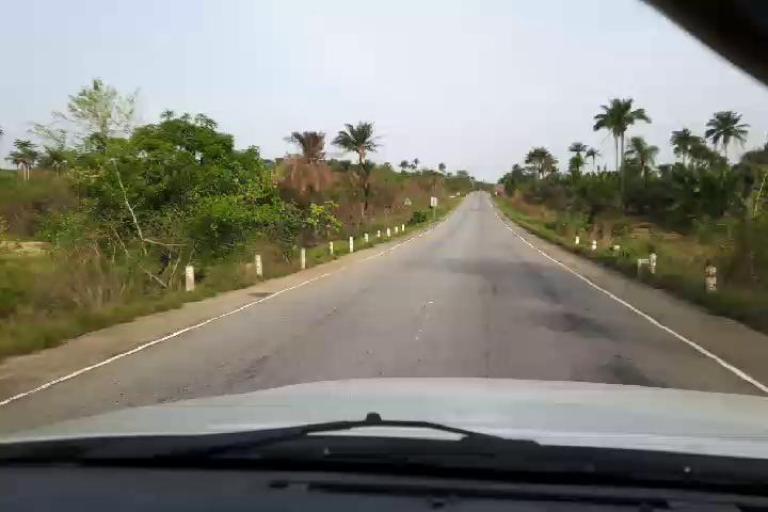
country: SL
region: Eastern Province
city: Blama
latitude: 7.9134
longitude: -11.4184
